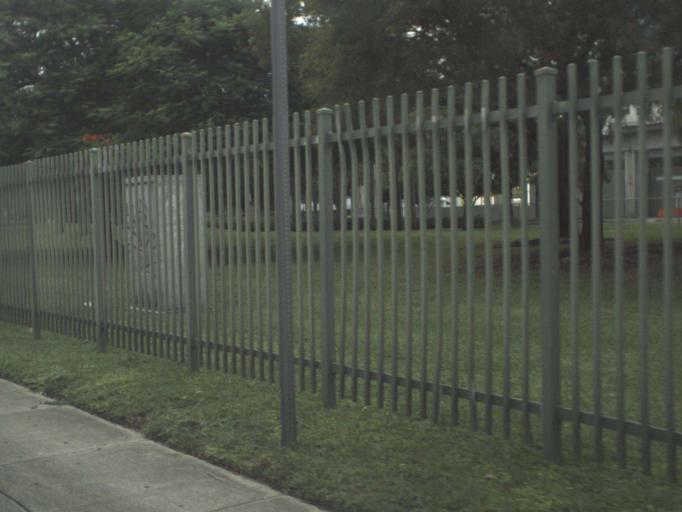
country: US
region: Florida
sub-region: Miami-Dade County
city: Coral Gables
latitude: 25.7321
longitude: -80.2547
